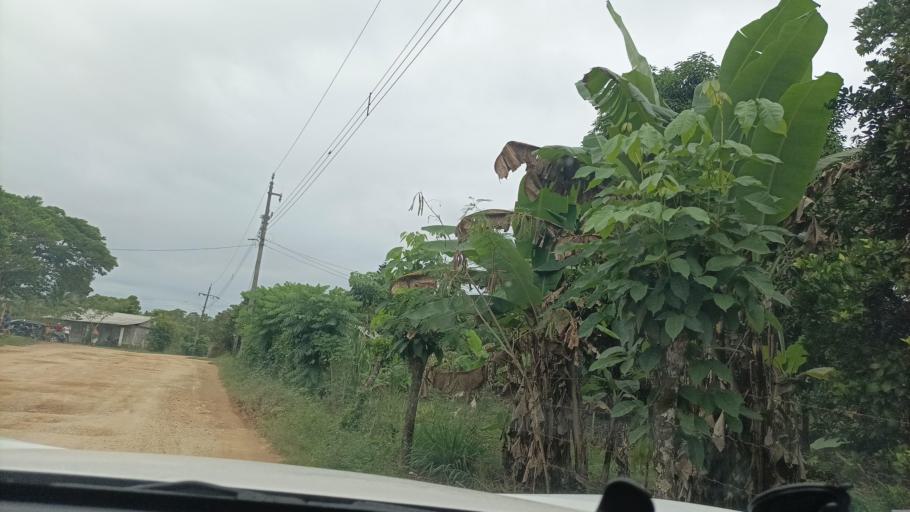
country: MX
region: Veracruz
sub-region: Uxpanapa
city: Poblado Cinco
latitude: 17.4846
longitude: -94.5742
